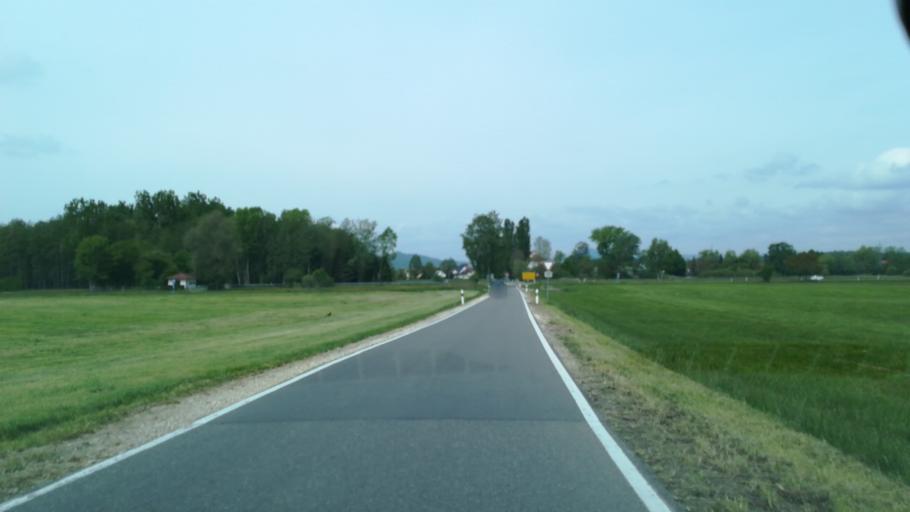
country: DE
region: Baden-Wuerttemberg
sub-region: Freiburg Region
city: Volkertshausen
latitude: 47.7989
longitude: 8.8831
